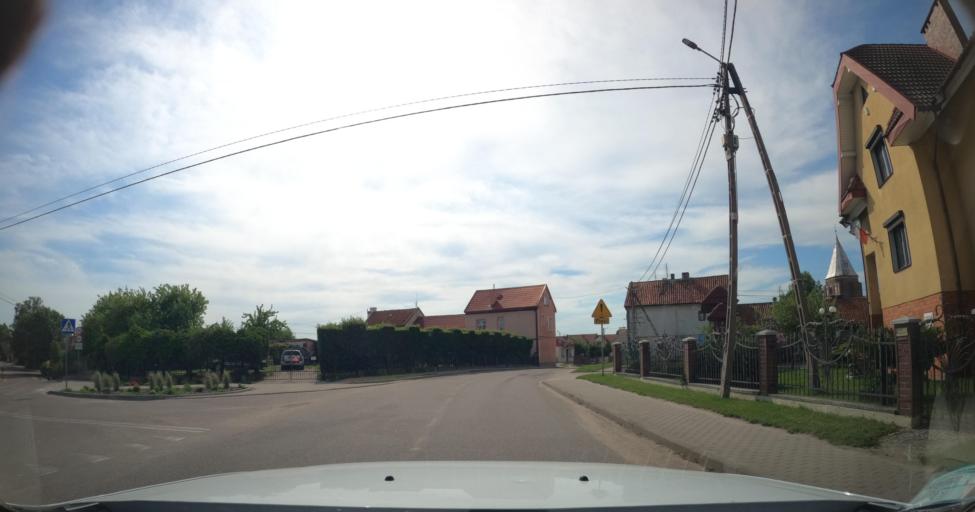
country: PL
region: Warmian-Masurian Voivodeship
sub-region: Powiat ostrodzki
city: Milakowo
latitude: 54.0097
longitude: 20.0744
